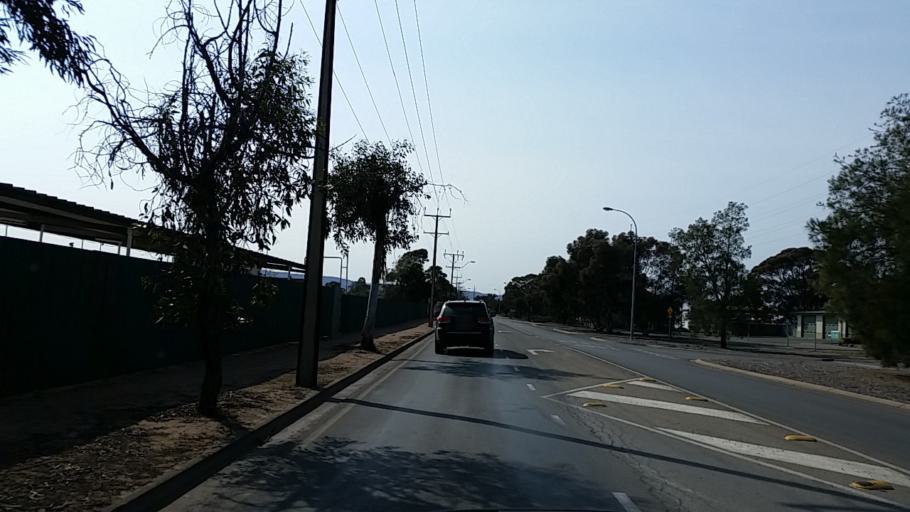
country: AU
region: South Australia
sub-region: Port Pirie City and Dists
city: Port Pirie
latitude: -33.1893
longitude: 138.0049
